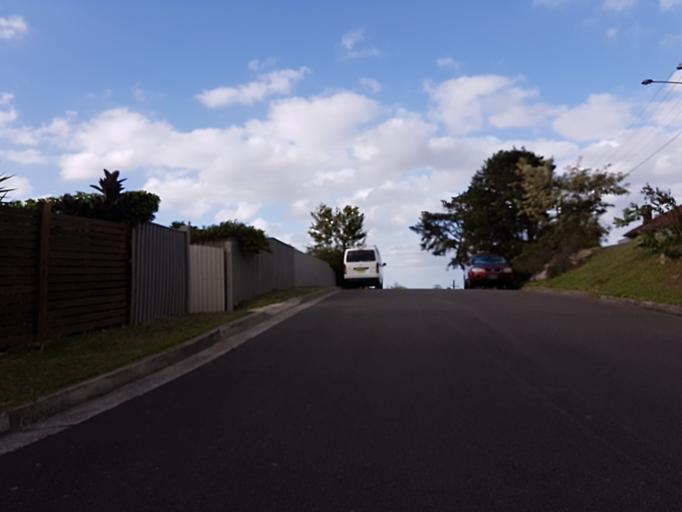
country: AU
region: New South Wales
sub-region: Manly Vale
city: Balgowlah
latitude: -33.7954
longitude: 151.2462
